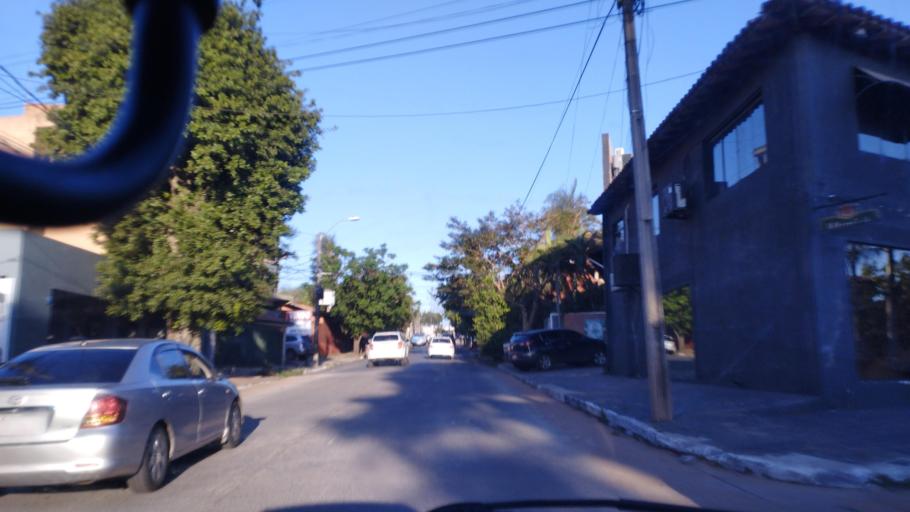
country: PY
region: Asuncion
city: Asuncion
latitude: -25.3010
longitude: -57.5929
